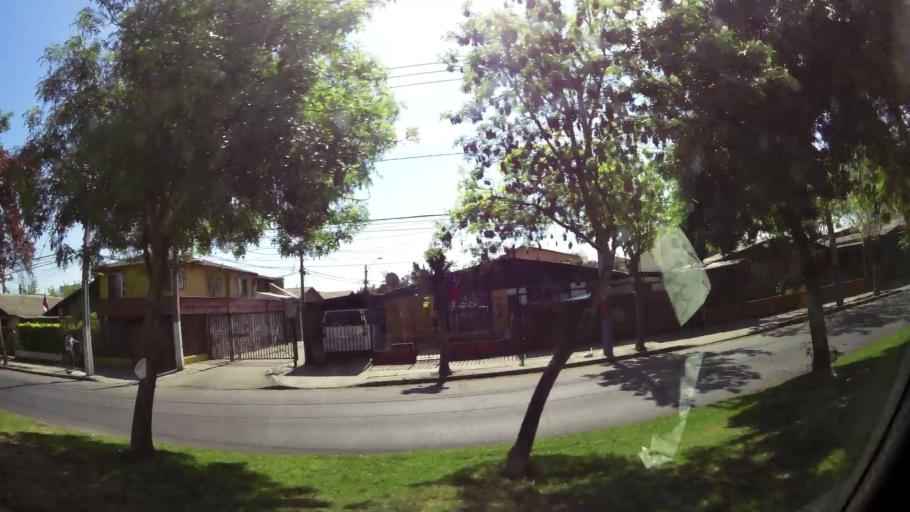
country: CL
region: Santiago Metropolitan
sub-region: Provincia de Santiago
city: Lo Prado
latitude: -33.4908
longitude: -70.7397
